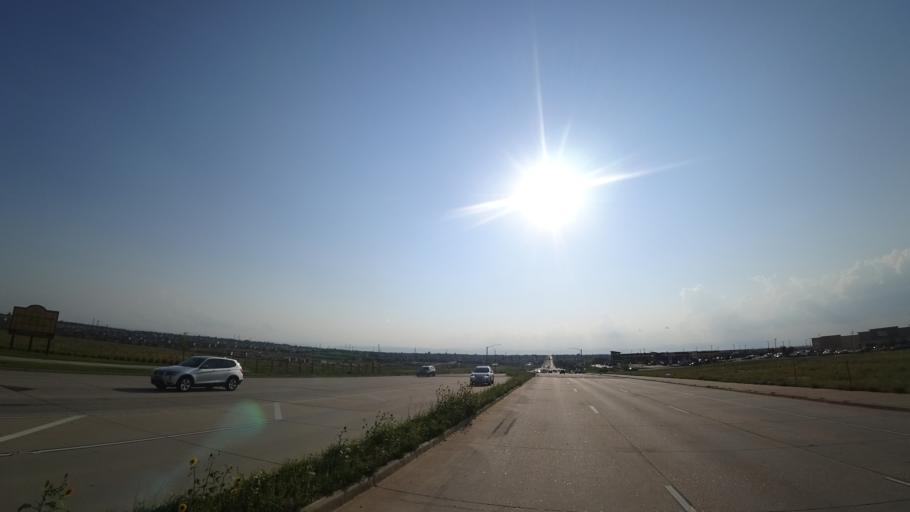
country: US
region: Colorado
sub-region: Arapahoe County
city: Dove Valley
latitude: 39.6385
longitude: -104.7354
